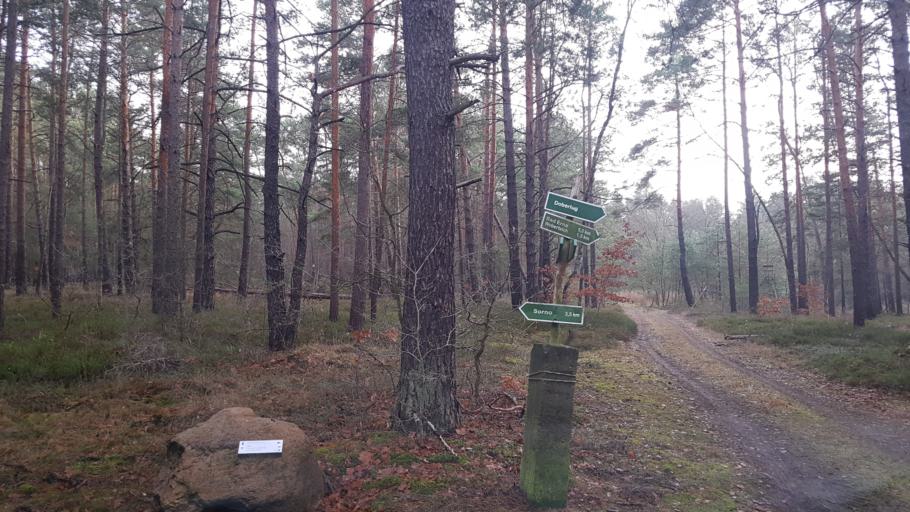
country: DE
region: Brandenburg
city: Ruckersdorf
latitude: 51.5845
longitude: 13.6212
